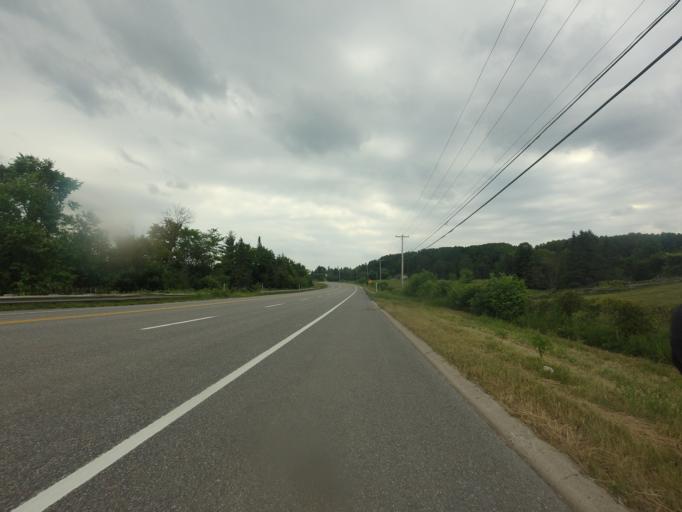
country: CA
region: Quebec
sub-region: Outaouais
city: Wakefield
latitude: 45.7171
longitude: -75.9153
